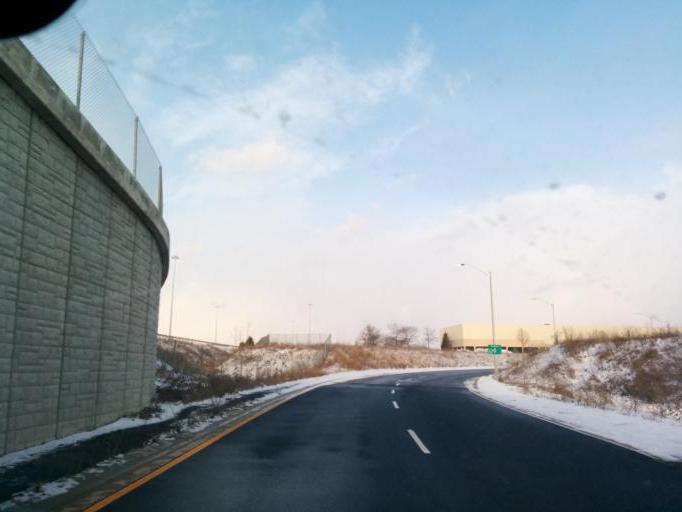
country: CA
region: Ontario
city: Mississauga
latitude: 43.6295
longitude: -79.6819
